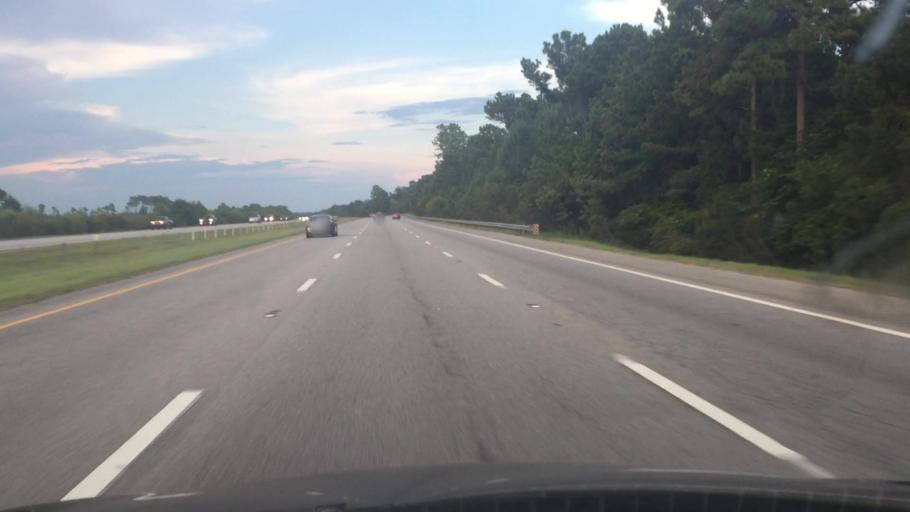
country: US
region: South Carolina
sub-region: Horry County
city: Myrtle Beach
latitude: 33.7693
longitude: -78.8259
